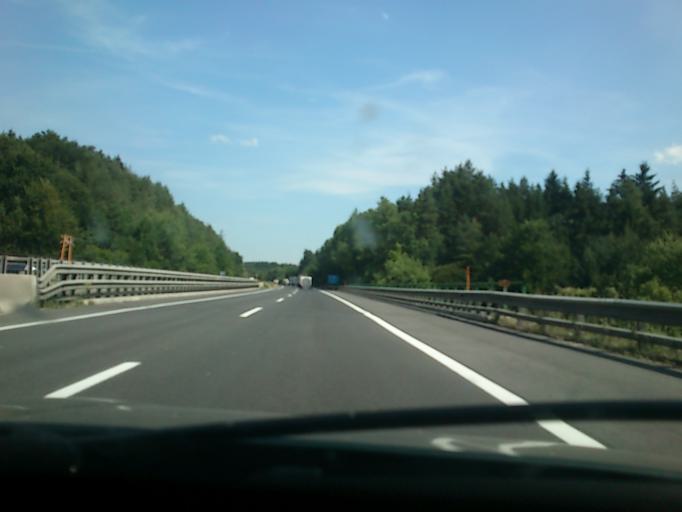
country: AT
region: Lower Austria
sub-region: Politischer Bezirk Neunkirchen
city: Seebenstein
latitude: 47.6886
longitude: 16.1275
